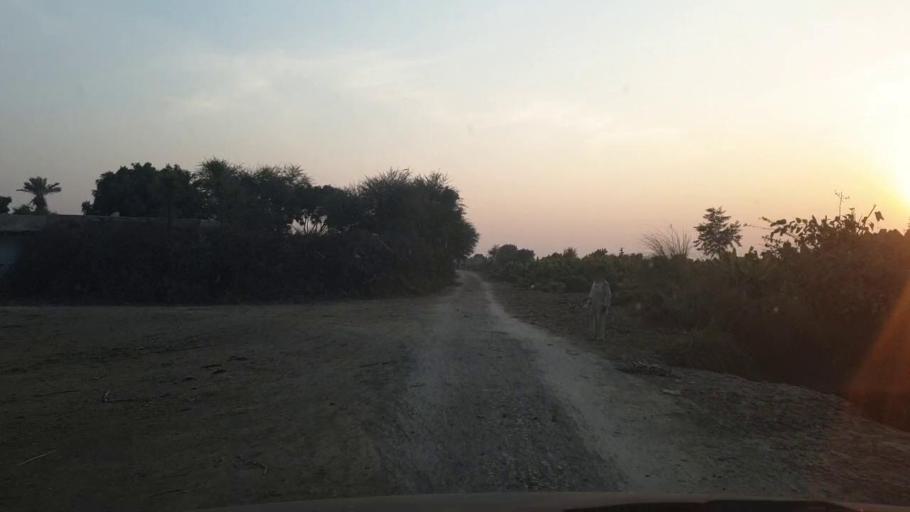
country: PK
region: Sindh
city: Bhit Shah
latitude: 25.8620
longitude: 68.5176
